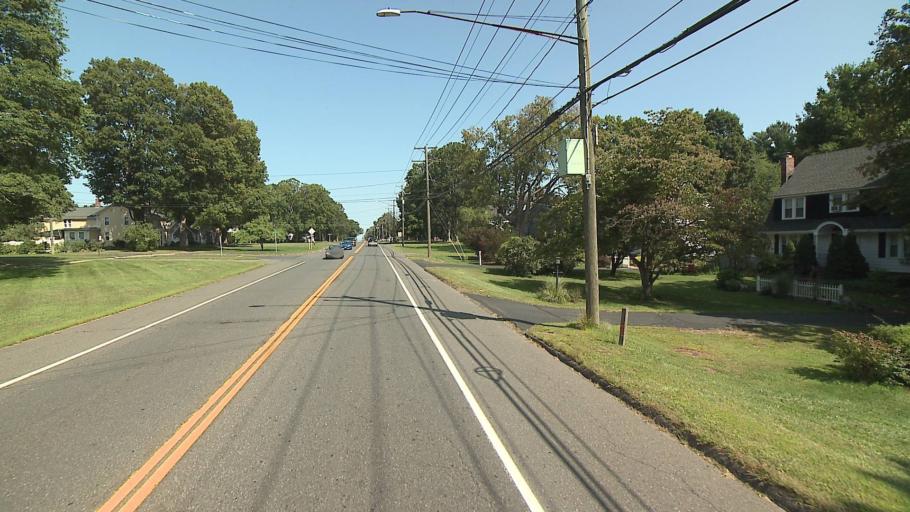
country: US
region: Connecticut
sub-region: Hartford County
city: Enfield
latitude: 41.9804
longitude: -72.5923
